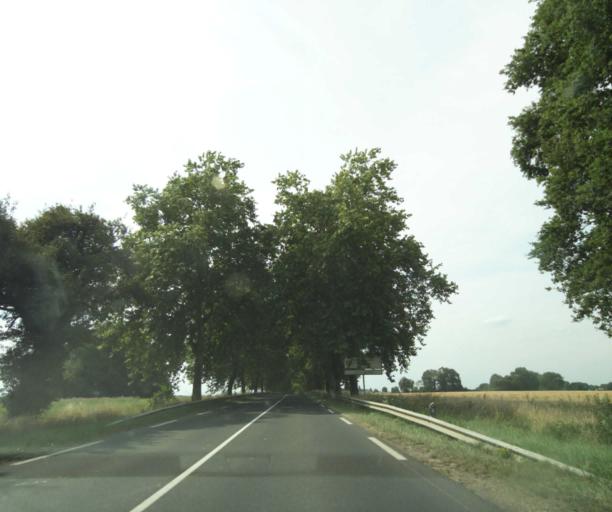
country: FR
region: Centre
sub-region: Departement d'Indre-et-Loire
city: Neuille-Pont-Pierre
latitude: 47.5899
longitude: 0.5363
